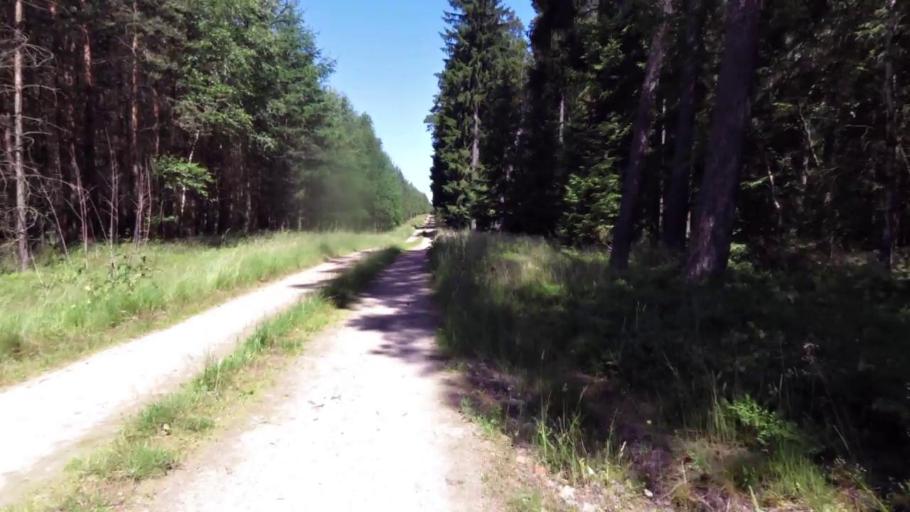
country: PL
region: West Pomeranian Voivodeship
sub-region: Powiat bialogardzki
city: Tychowo
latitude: 53.9163
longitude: 16.1233
